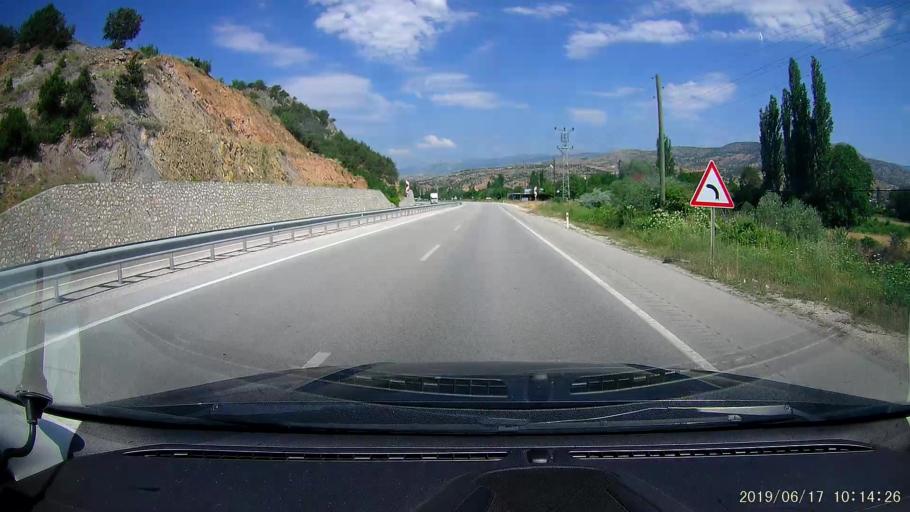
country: TR
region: Amasya
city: Saraycik
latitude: 40.9909
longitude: 35.0264
